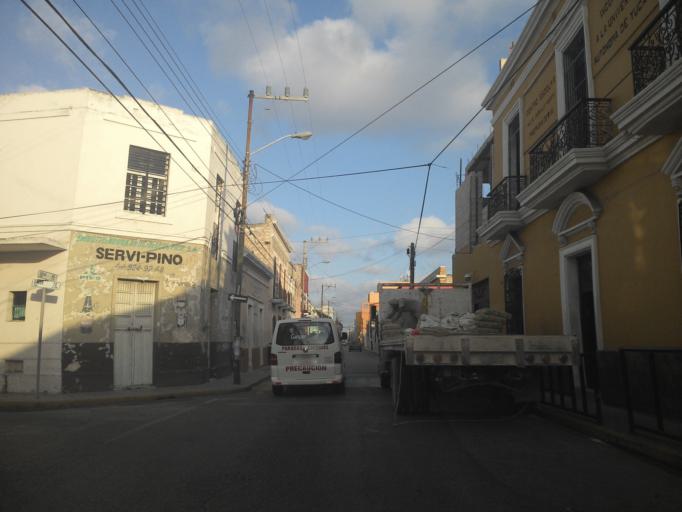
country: MX
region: Yucatan
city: Merida
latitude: 20.9677
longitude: -89.6314
